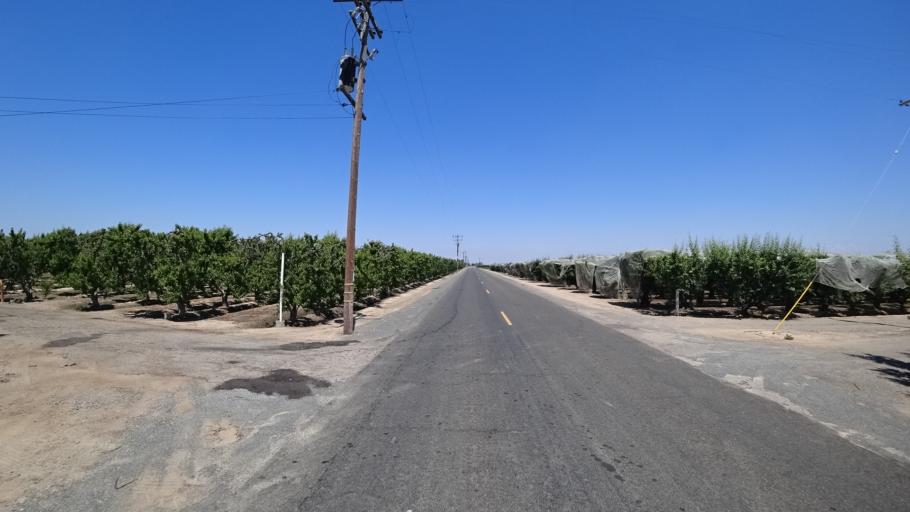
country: US
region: California
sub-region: Fresno County
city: Kingsburg
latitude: 36.4707
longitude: -119.6002
